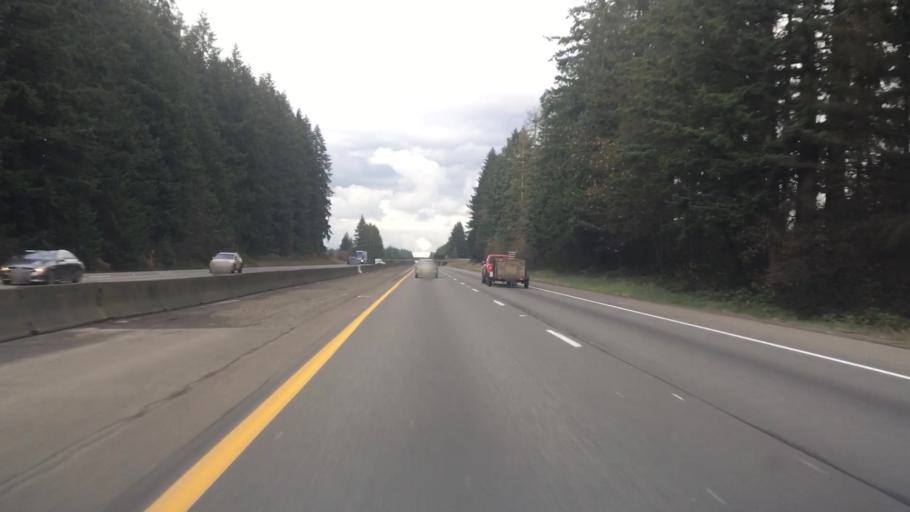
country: US
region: Washington
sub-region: Lewis County
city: Winlock
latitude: 46.5128
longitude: -122.8766
